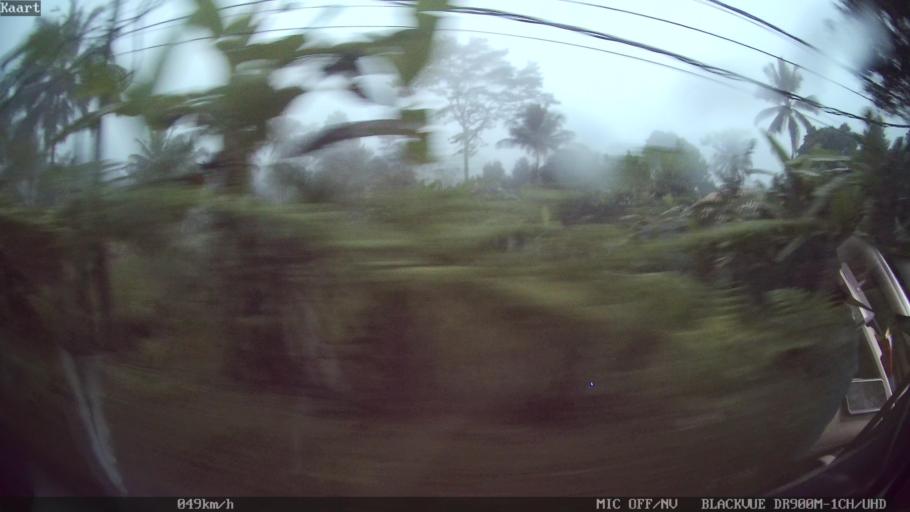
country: ID
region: Bali
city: Banjar Taro Kelod
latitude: -8.3484
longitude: 115.2784
